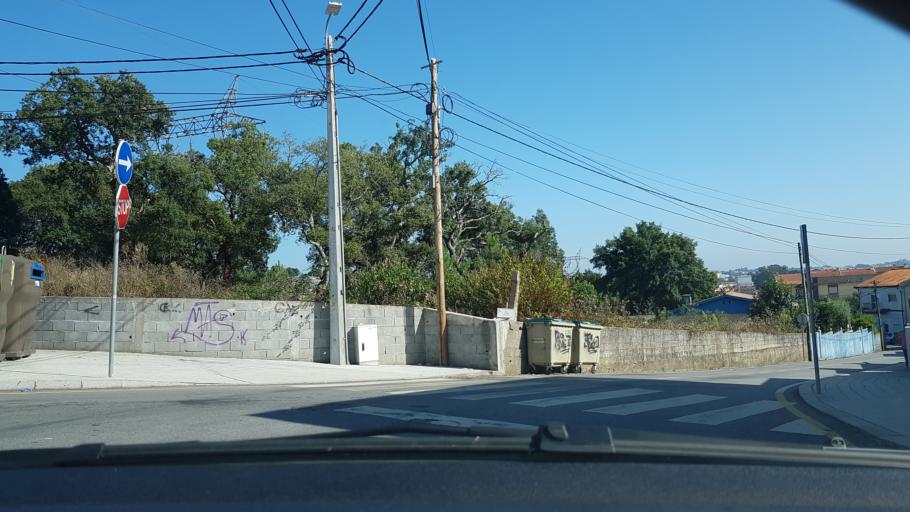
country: PT
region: Porto
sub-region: Gondomar
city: Baguim do Monte
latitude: 41.1889
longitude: -8.5349
